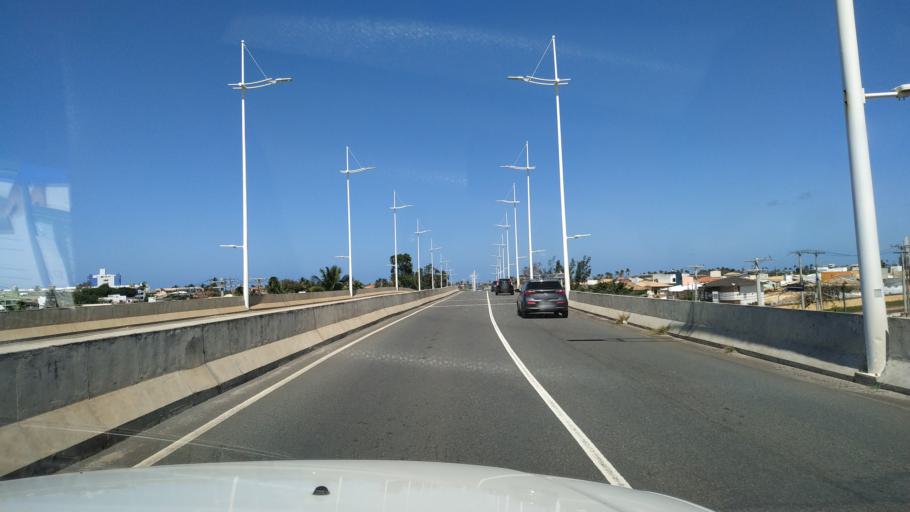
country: BR
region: Bahia
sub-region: Lauro De Freitas
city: Lauro de Freitas
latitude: -12.9479
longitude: -38.3844
